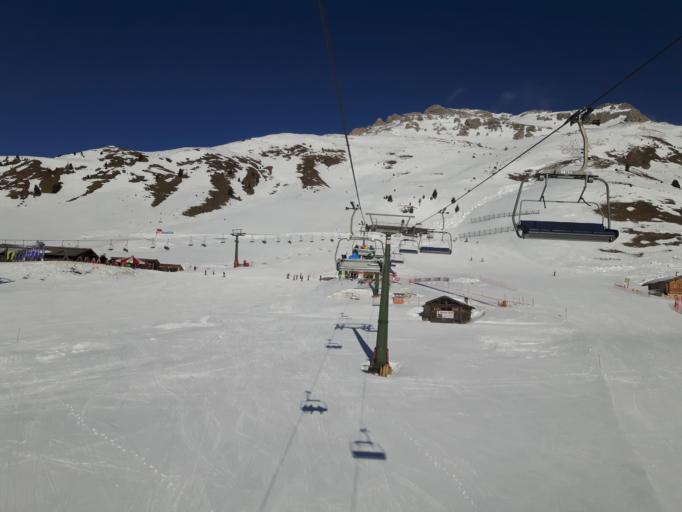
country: IT
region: Trentino-Alto Adige
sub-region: Provincia di Trento
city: Panchia
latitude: 46.3493
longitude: 11.5464
